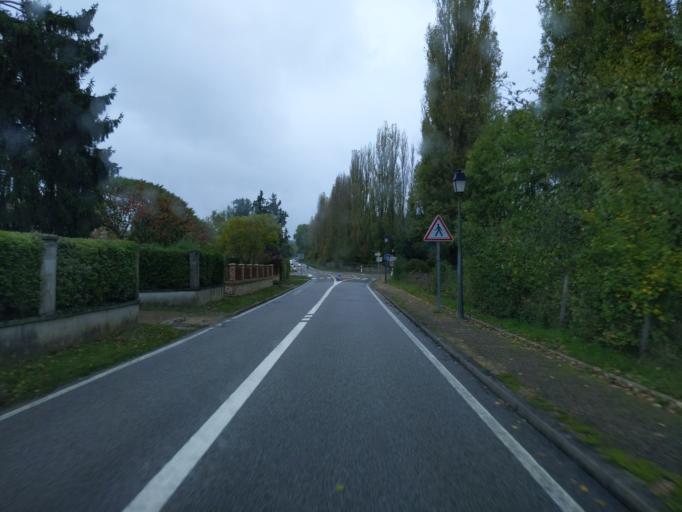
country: FR
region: Ile-de-France
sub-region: Departement des Yvelines
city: Dampierre-en-Yvelines
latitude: 48.6900
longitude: 1.9740
